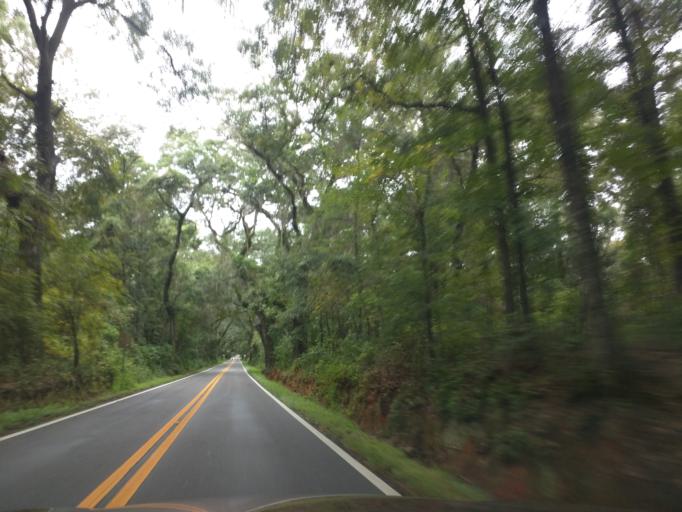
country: US
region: Florida
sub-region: Leon County
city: Tallahassee
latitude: 30.4881
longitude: -84.1905
